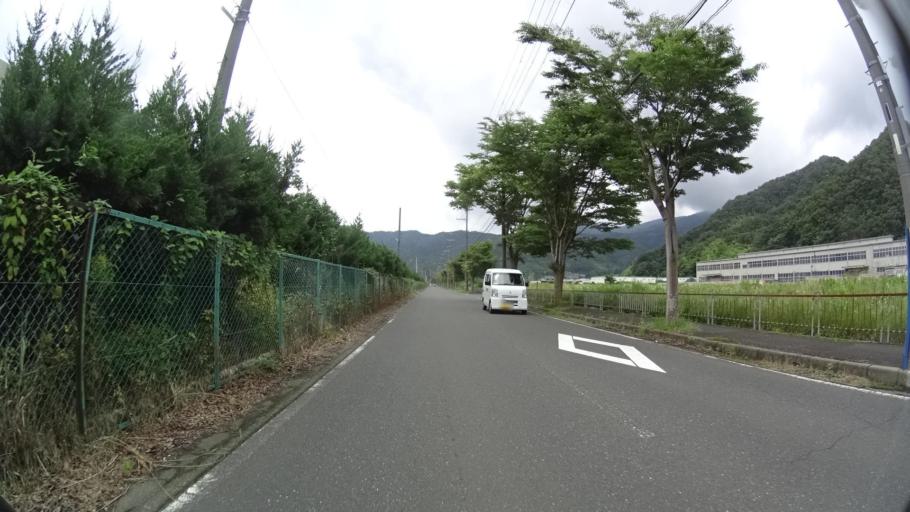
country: JP
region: Kyoto
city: Maizuru
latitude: 35.5049
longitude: 135.3809
